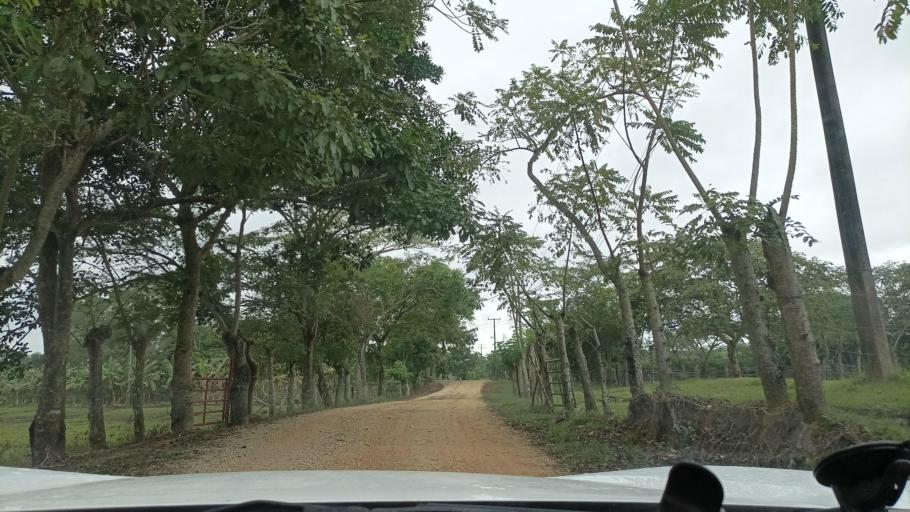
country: MX
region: Veracruz
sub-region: Moloacan
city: Cuichapa
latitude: 17.7811
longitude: -94.3889
